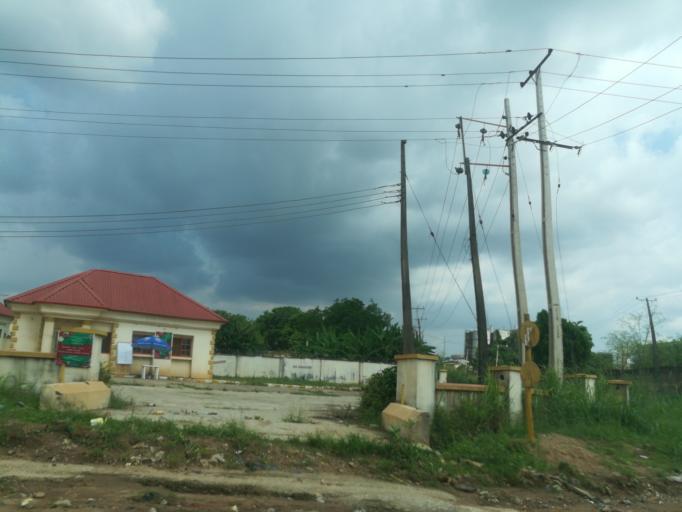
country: NG
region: Oyo
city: Ibadan
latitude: 7.3590
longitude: 3.8457
